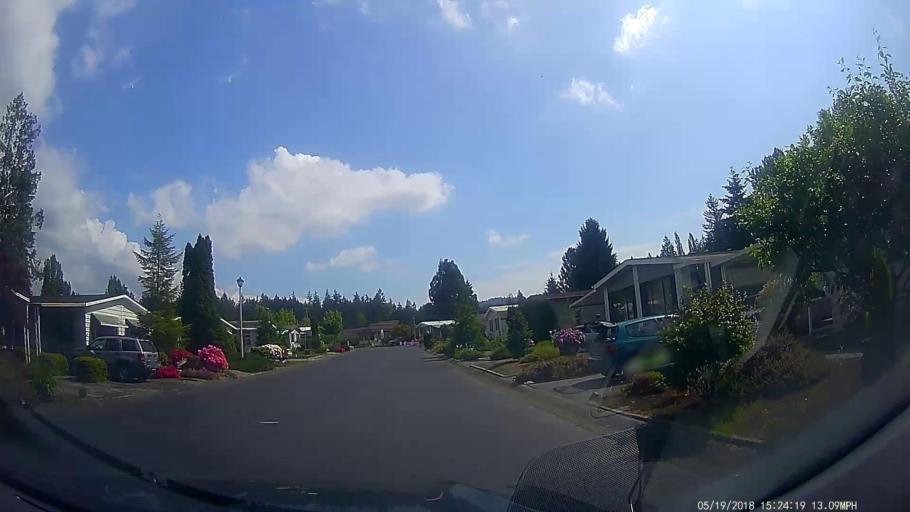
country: US
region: Washington
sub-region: Skagit County
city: Mount Vernon
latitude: 48.4306
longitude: -122.3045
